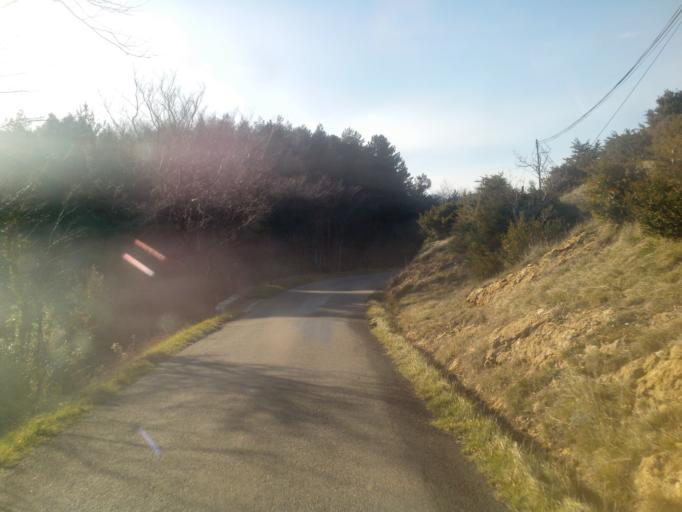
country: FR
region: Languedoc-Roussillon
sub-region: Departement de l'Aude
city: Couiza
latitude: 42.8787
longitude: 2.3759
